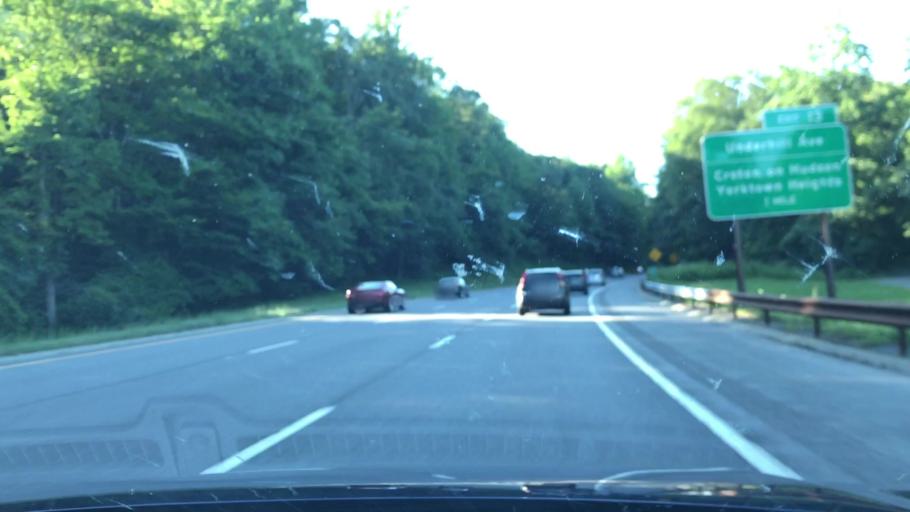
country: US
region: New York
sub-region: Westchester County
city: Yorktown Heights
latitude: 41.2335
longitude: -73.8119
